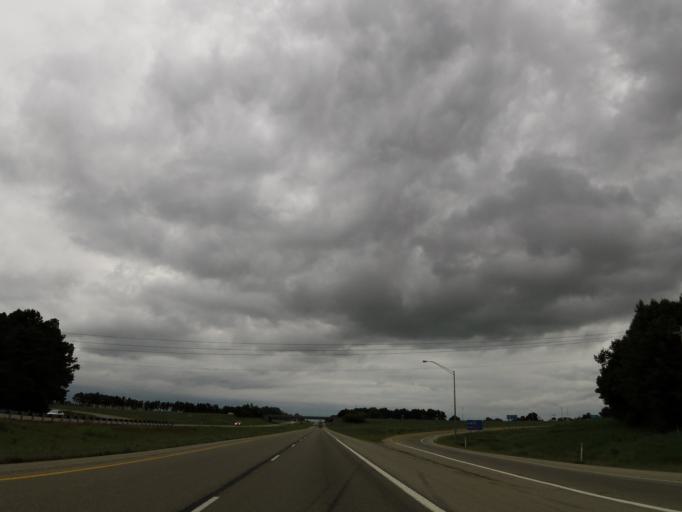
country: US
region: Illinois
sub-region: Massac County
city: Metropolis
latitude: 37.1571
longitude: -88.6825
